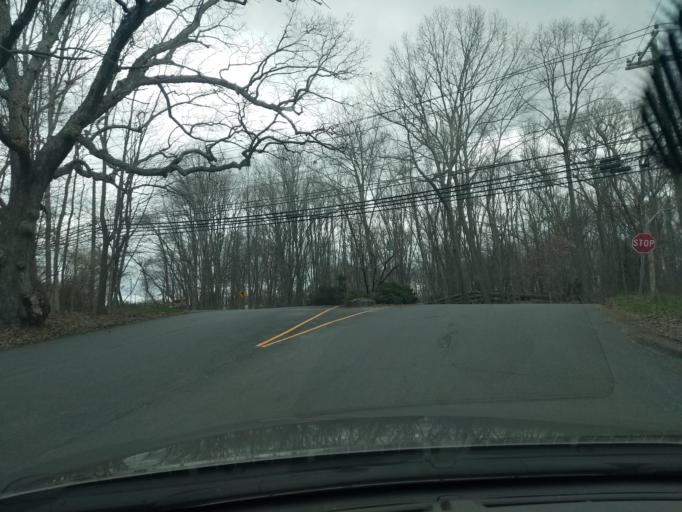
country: US
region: Connecticut
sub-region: Fairfield County
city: Newtown
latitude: 41.3788
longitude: -73.2824
